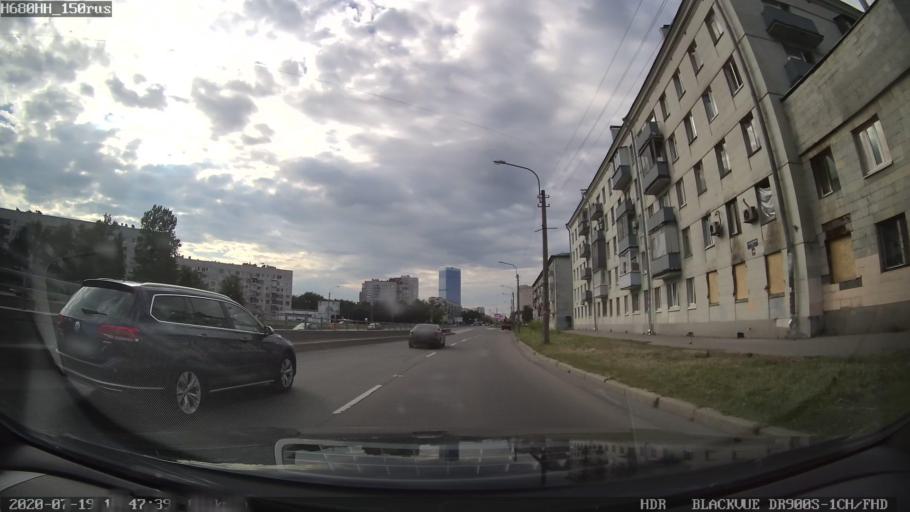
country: RU
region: St.-Petersburg
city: Kupchino
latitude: 59.8446
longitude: 30.3194
